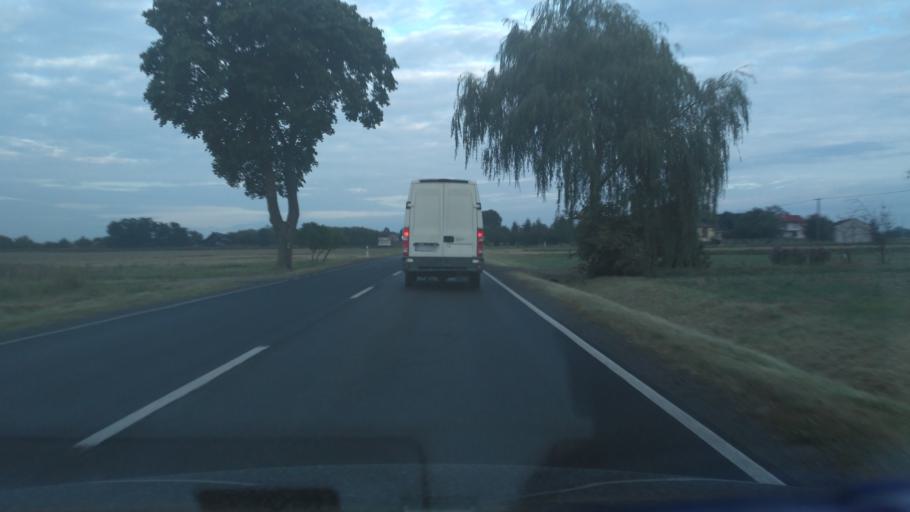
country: PL
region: Lublin Voivodeship
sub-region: Powiat leczynski
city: Spiczyn
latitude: 51.2990
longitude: 22.7653
